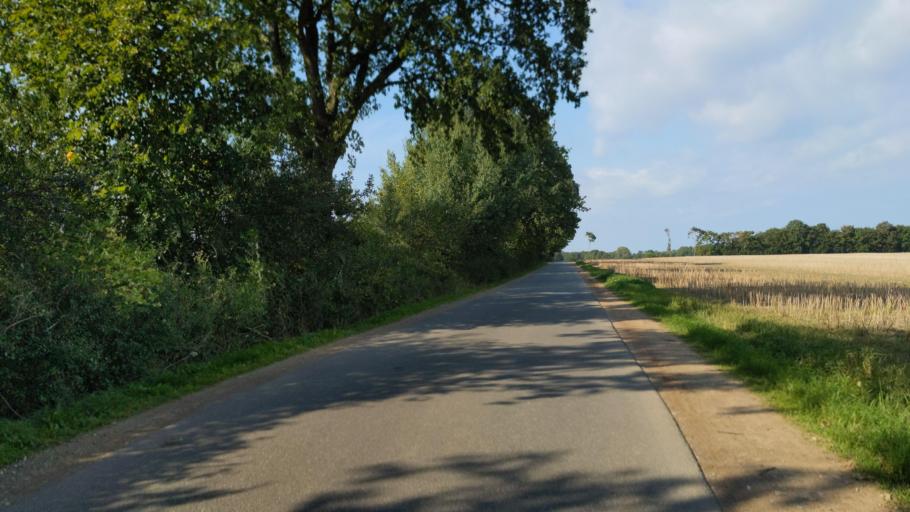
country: DE
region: Mecklenburg-Vorpommern
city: Kalkhorst
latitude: 53.9696
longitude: 11.0100
